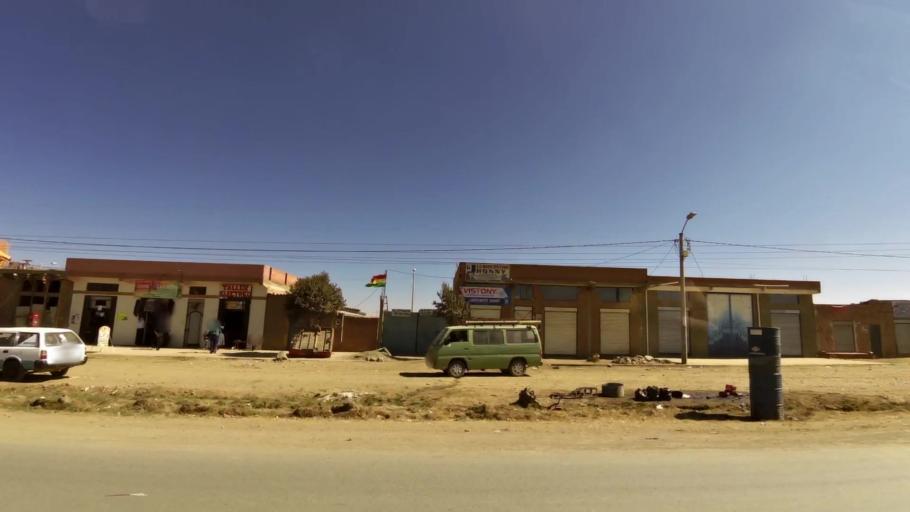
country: BO
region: La Paz
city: La Paz
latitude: -16.5780
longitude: -68.2308
